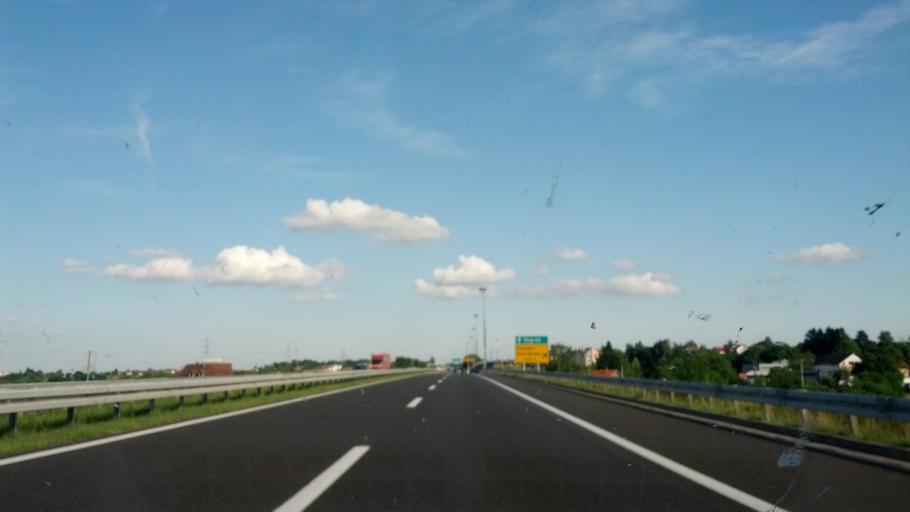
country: HR
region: Zagrebacka
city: Bestovje
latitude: 45.8020
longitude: 15.7789
